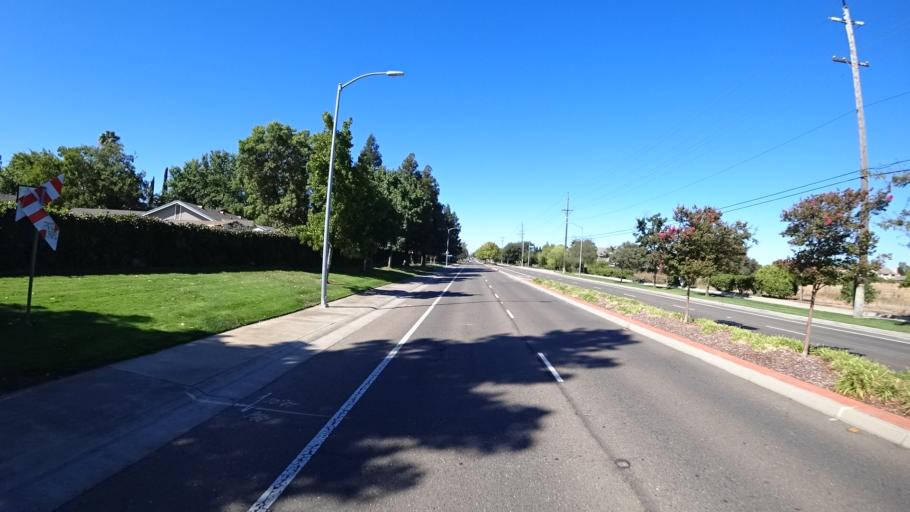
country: US
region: California
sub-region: Sacramento County
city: Elk Grove
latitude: 38.4235
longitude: -121.3607
